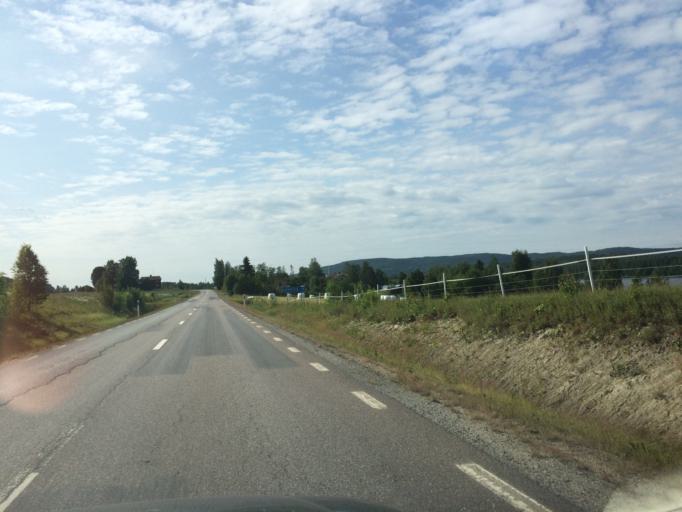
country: SE
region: Vaesternorrland
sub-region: Kramfors Kommun
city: Bollstabruk
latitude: 63.0811
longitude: 17.7754
